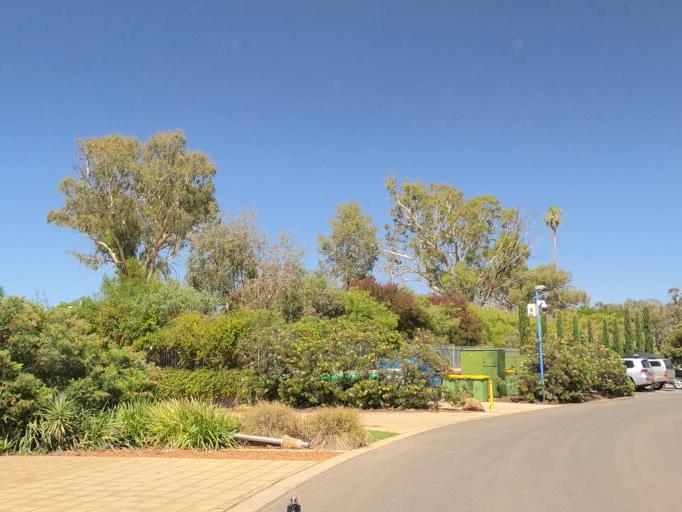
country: AU
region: New South Wales
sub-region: Corowa Shire
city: Mulwala
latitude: -36.0012
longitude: 146.0032
